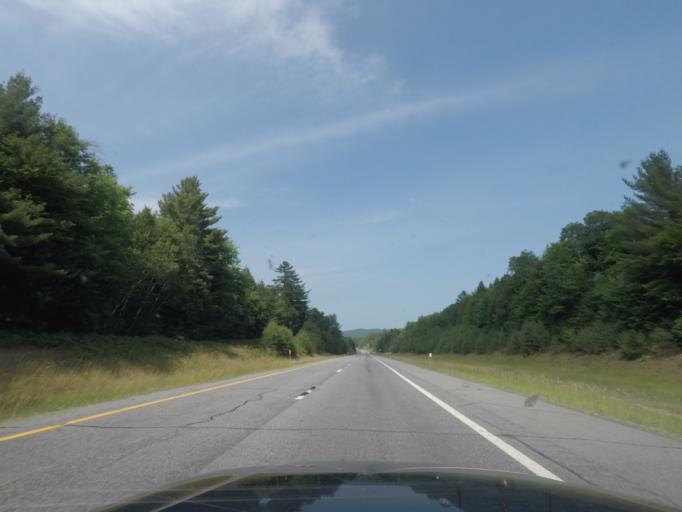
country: US
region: New York
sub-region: Essex County
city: Mineville
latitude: 44.1164
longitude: -73.6030
